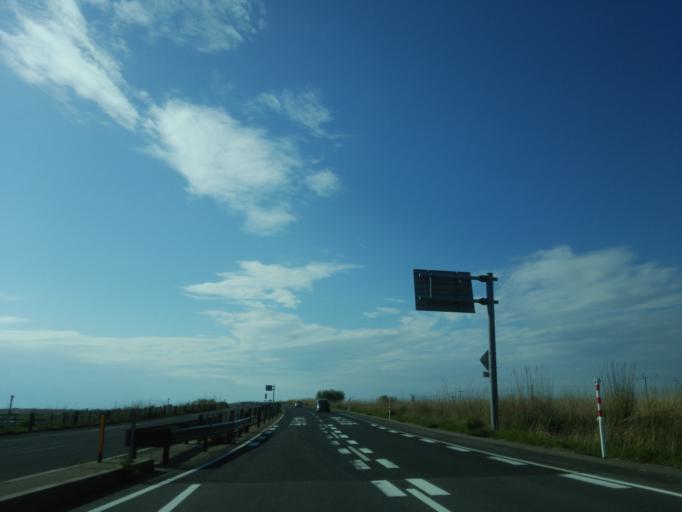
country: JP
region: Niigata
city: Kameda-honcho
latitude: 37.8486
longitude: 139.1416
